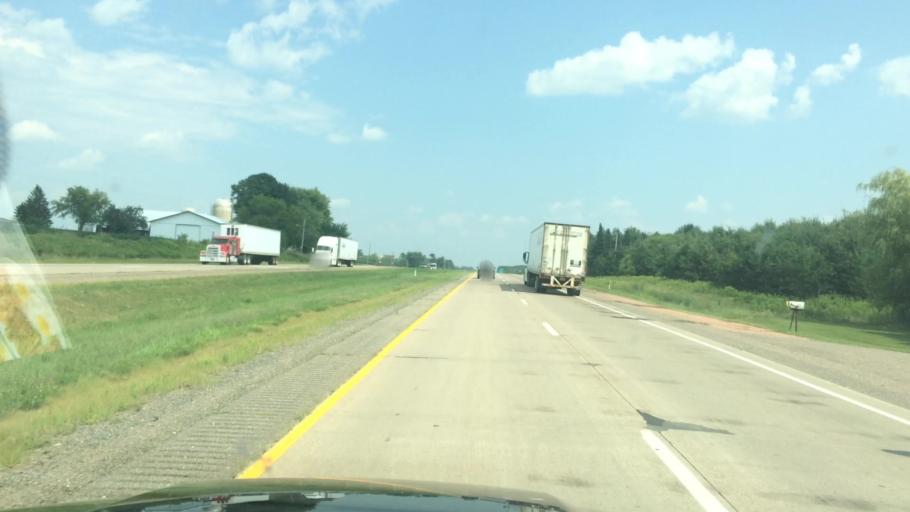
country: US
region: Wisconsin
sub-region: Marathon County
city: Athens
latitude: 44.9456
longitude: -90.1163
